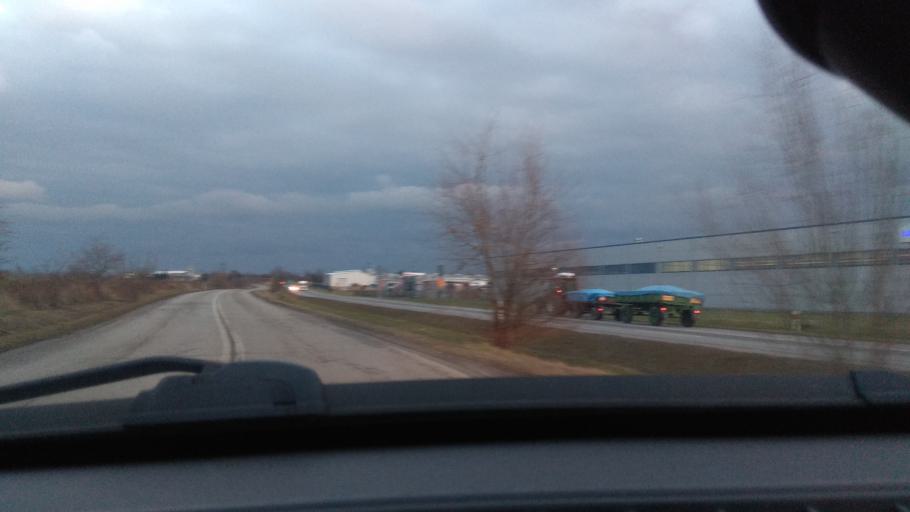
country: PL
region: Greater Poland Voivodeship
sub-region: Powiat kepinski
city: Kepno
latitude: 51.2885
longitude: 18.0062
